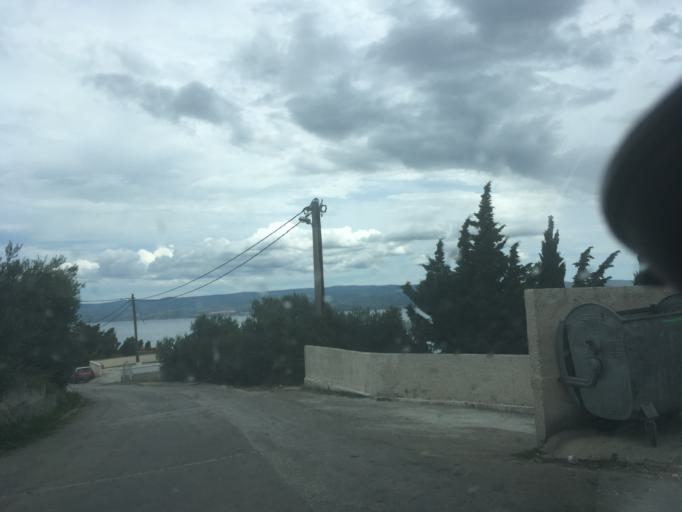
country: HR
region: Splitsko-Dalmatinska
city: Jesenice
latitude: 43.4540
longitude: 16.6239
